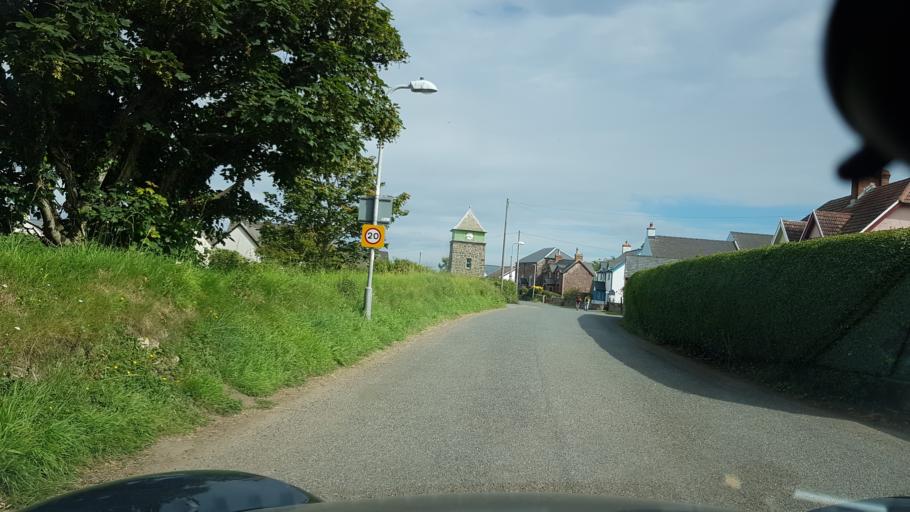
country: GB
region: Wales
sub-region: Pembrokeshire
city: Dale
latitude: 51.7316
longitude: -5.1977
